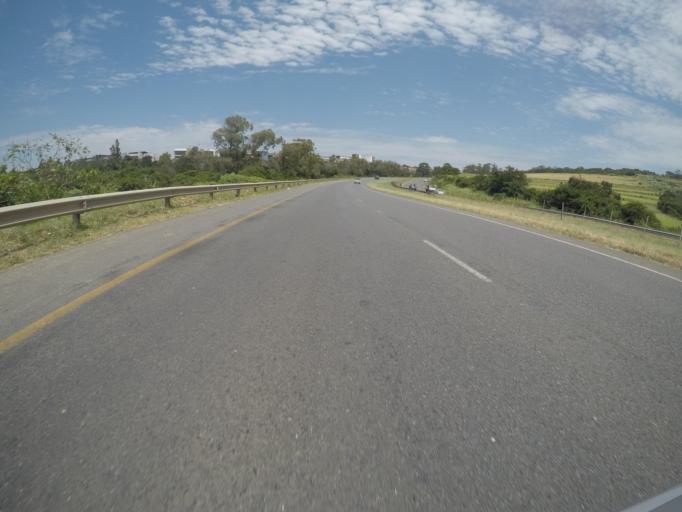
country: ZA
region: Eastern Cape
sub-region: Buffalo City Metropolitan Municipality
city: East London
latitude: -32.9454
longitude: 27.9416
